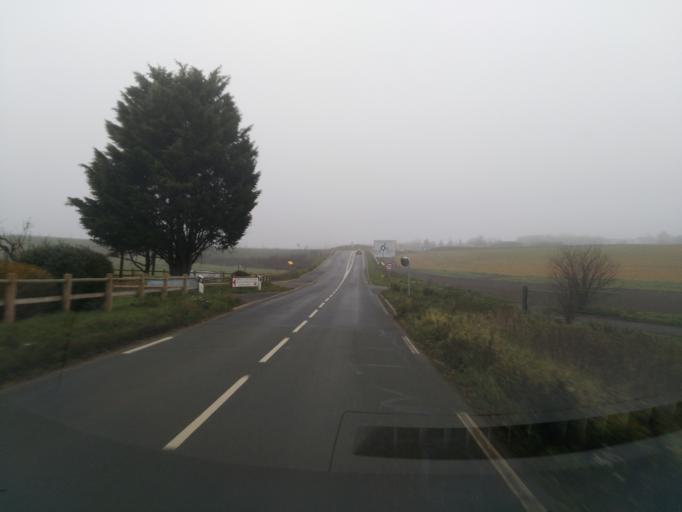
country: FR
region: Ile-de-France
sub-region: Departement des Yvelines
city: Chavenay
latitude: 48.8575
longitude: 2.0039
